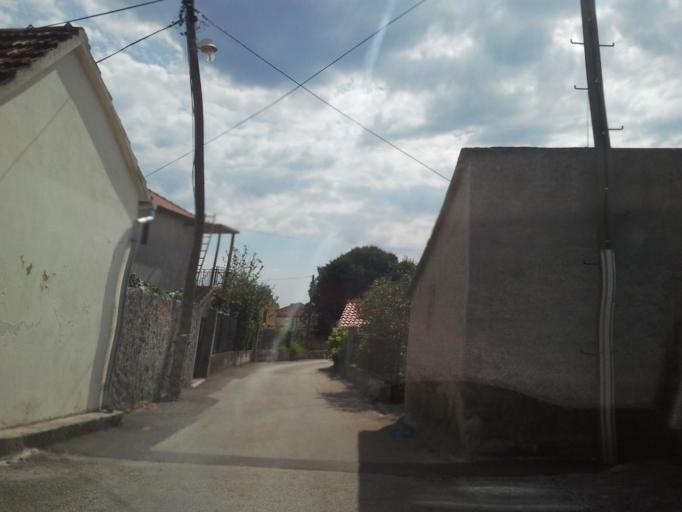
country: HR
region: Zadarska
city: Zadar
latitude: 44.1196
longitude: 15.2494
